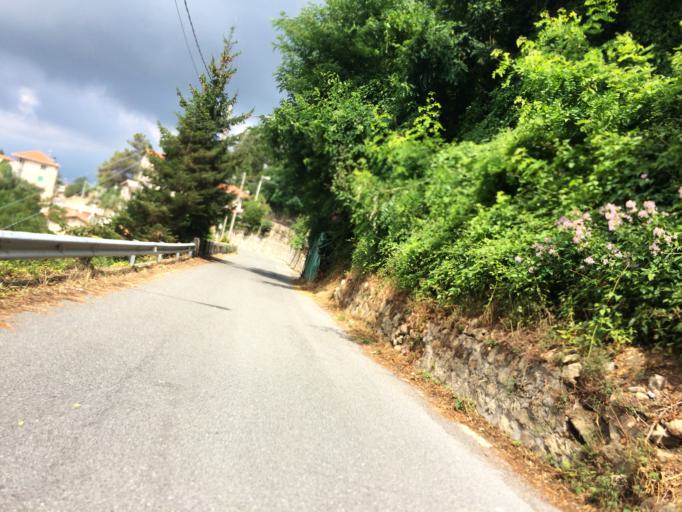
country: IT
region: Liguria
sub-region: Provincia di Imperia
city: Bajardo
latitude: 43.9027
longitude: 7.7259
